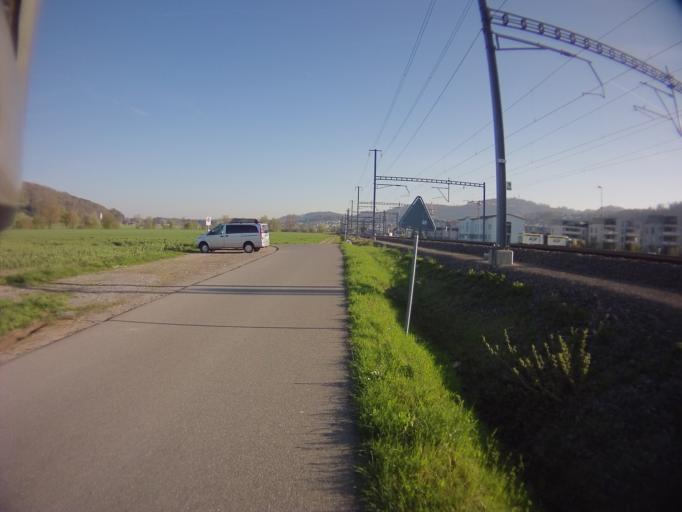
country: CH
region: Zurich
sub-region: Bezirk Affoltern
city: Schachen
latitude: 47.3221
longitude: 8.4671
